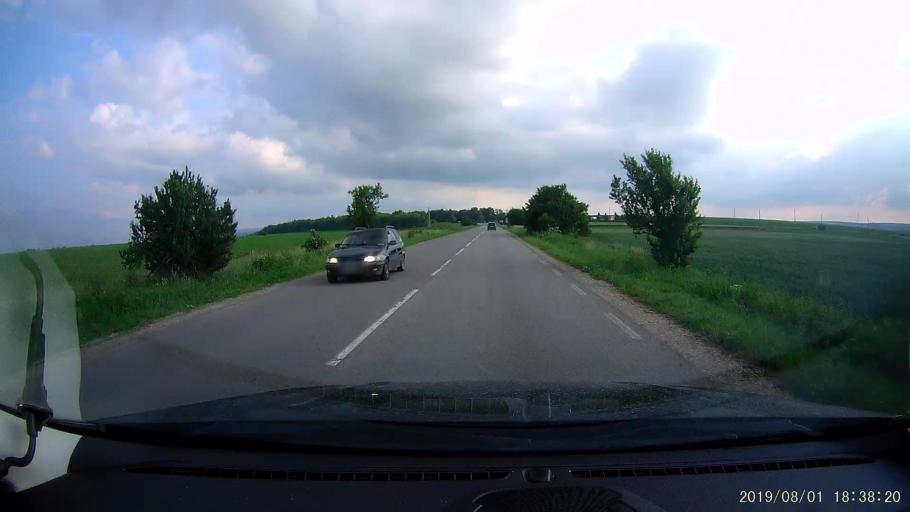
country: BG
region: Shumen
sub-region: Obshtina Khitrino
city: Gara Khitrino
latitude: 43.4038
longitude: 26.9181
